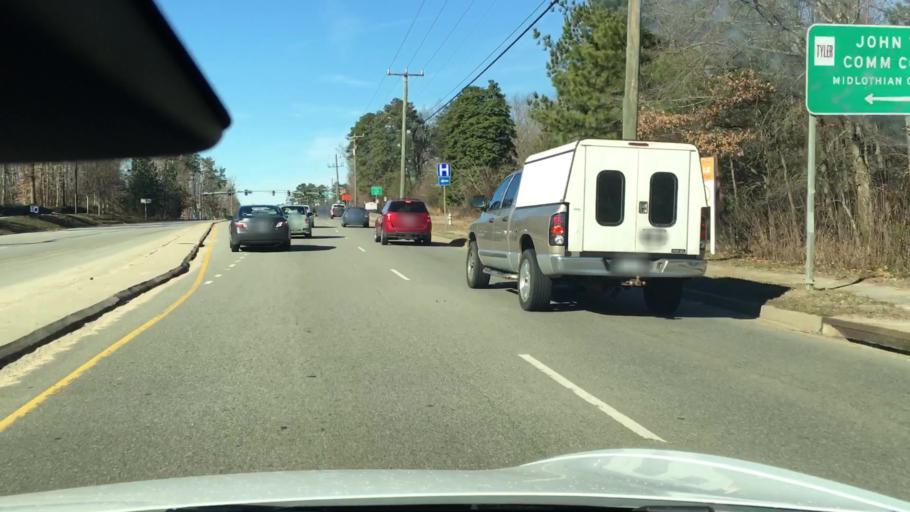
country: US
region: Virginia
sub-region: Chesterfield County
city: Brandermill
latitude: 37.5047
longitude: -77.6561
